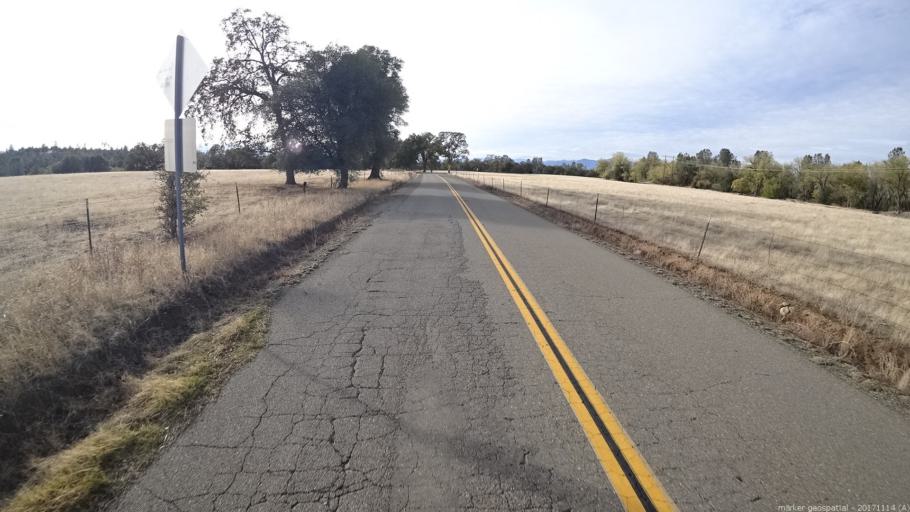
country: US
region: California
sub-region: Shasta County
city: Shasta
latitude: 40.3919
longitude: -122.5039
